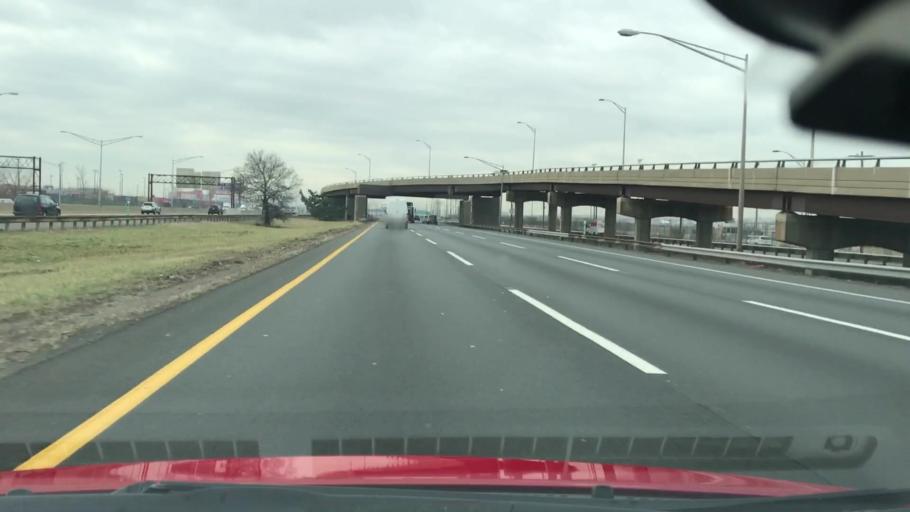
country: US
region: New Jersey
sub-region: Essex County
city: Newark
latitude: 40.6989
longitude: -74.1566
